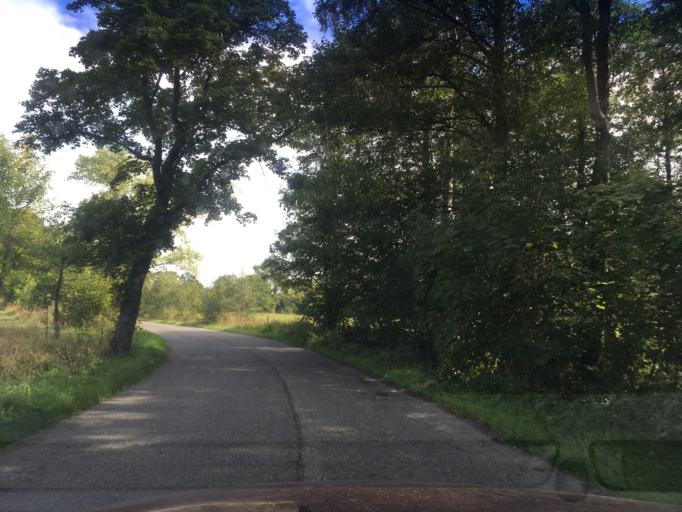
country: PL
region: Lower Silesian Voivodeship
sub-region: Powiat jeleniogorski
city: Stara Kamienica
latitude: 50.8808
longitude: 15.5569
